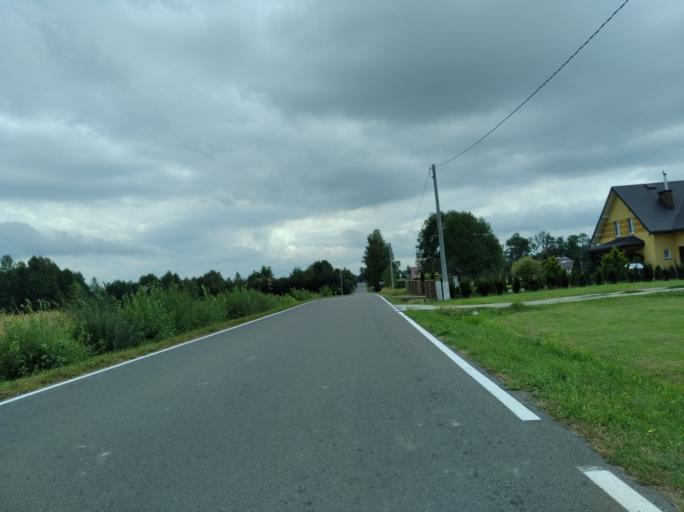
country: PL
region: Subcarpathian Voivodeship
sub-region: Powiat krosnienski
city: Odrzykon
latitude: 49.7450
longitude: 21.7282
